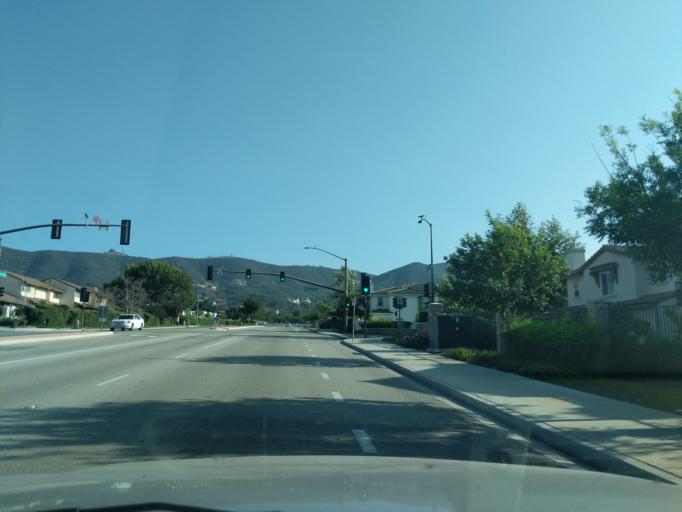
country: US
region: California
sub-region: Ventura County
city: Casa Conejo
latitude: 34.1808
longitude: -118.9113
